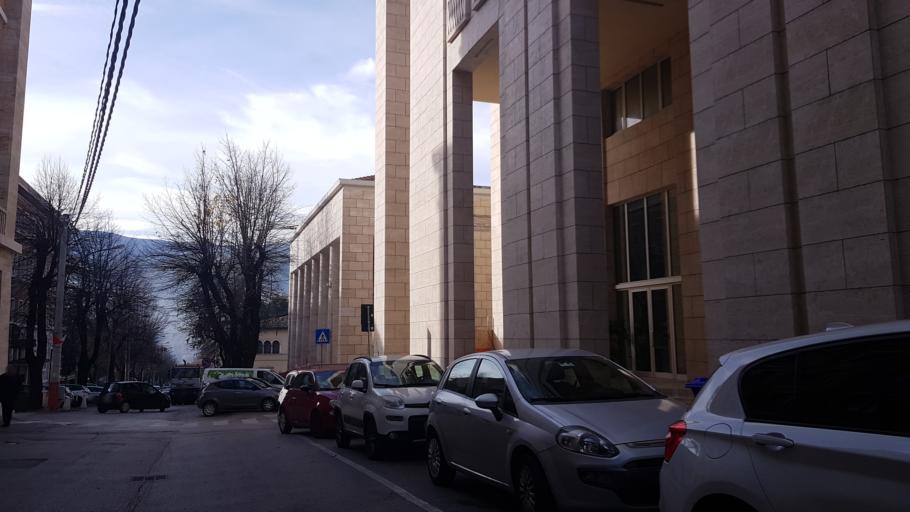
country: IT
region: Abruzzo
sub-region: Provincia dell' Aquila
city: L'Aquila
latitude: 42.3468
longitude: 13.3978
